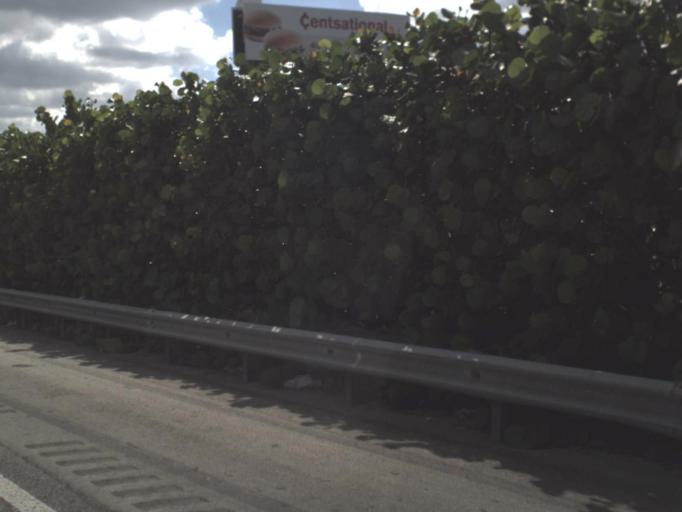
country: US
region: Florida
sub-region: Broward County
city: Davie
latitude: 26.0451
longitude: -80.2147
